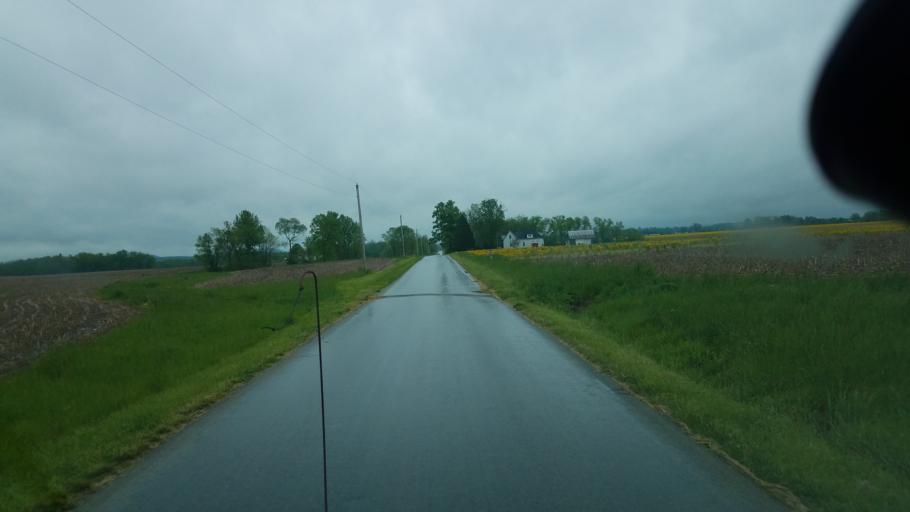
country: US
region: Ohio
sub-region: Highland County
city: Greenfield
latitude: 39.3298
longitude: -83.4310
